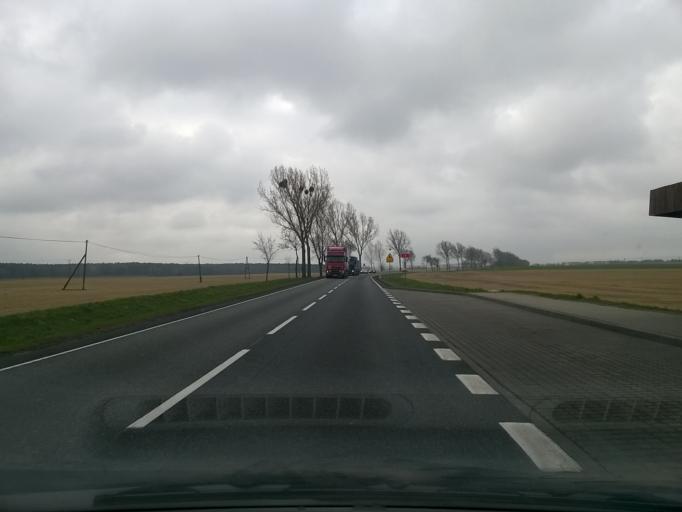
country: PL
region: Kujawsko-Pomorskie
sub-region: Powiat zninski
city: Znin
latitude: 52.9078
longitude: 17.7007
